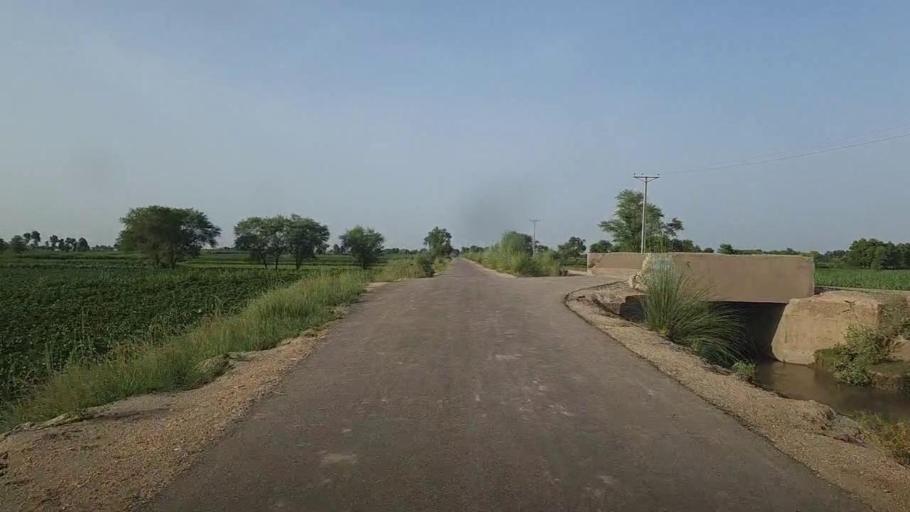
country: PK
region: Sindh
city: Ubauro
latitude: 28.0893
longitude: 69.8186
